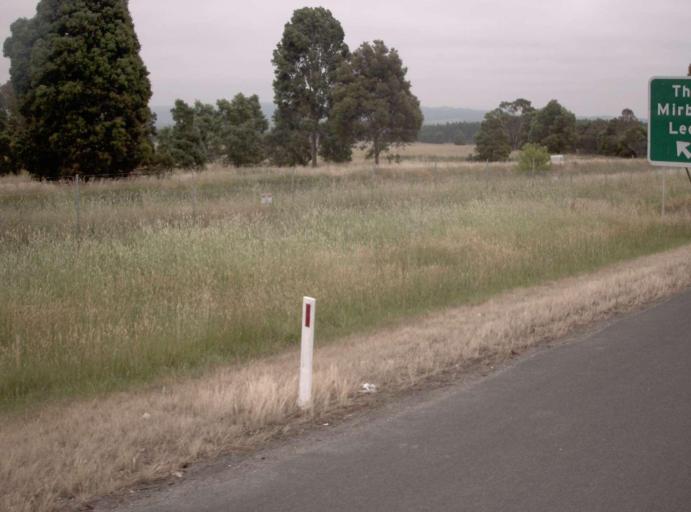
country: AU
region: Victoria
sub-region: Latrobe
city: Morwell
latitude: -38.2367
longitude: 146.3797
